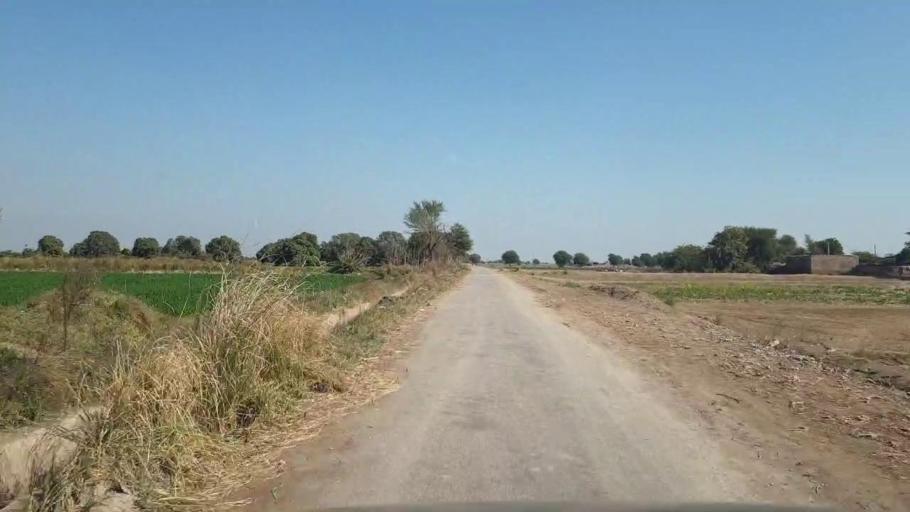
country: PK
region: Sindh
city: Shahpur Chakar
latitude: 26.1079
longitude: 68.6582
